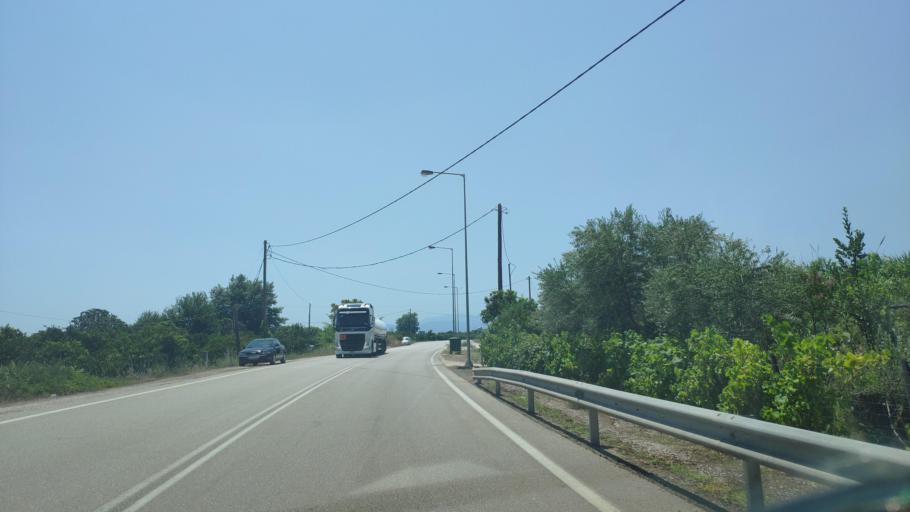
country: GR
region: Epirus
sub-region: Nomos Artas
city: Arta
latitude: 39.1369
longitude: 20.9836
